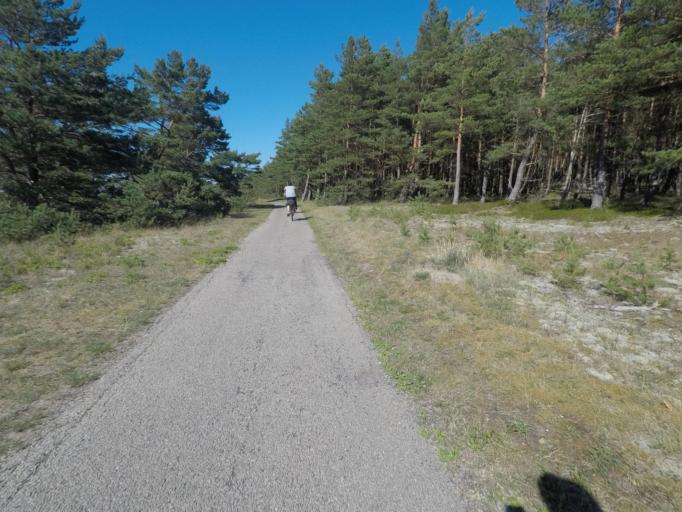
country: LT
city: Neringa
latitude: 55.4994
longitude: 21.0891
